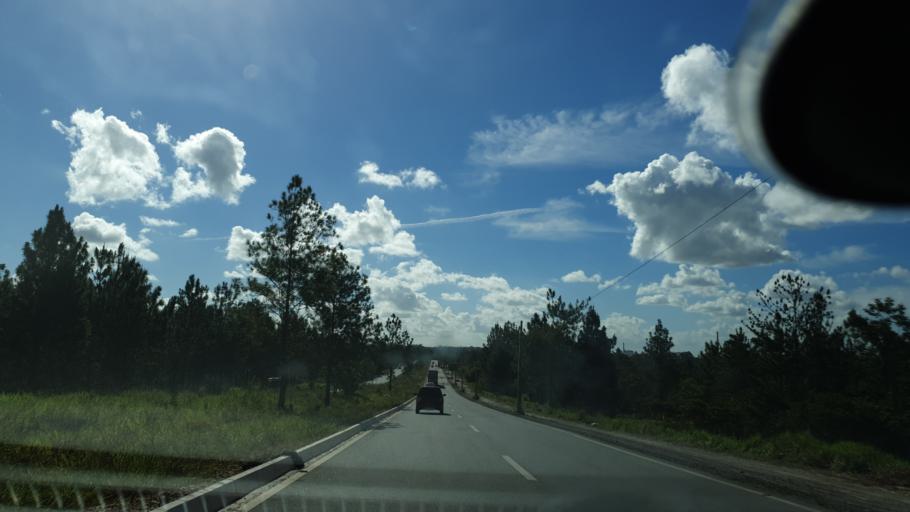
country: BR
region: Bahia
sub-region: Camacari
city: Camacari
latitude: -12.6825
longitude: -38.2926
